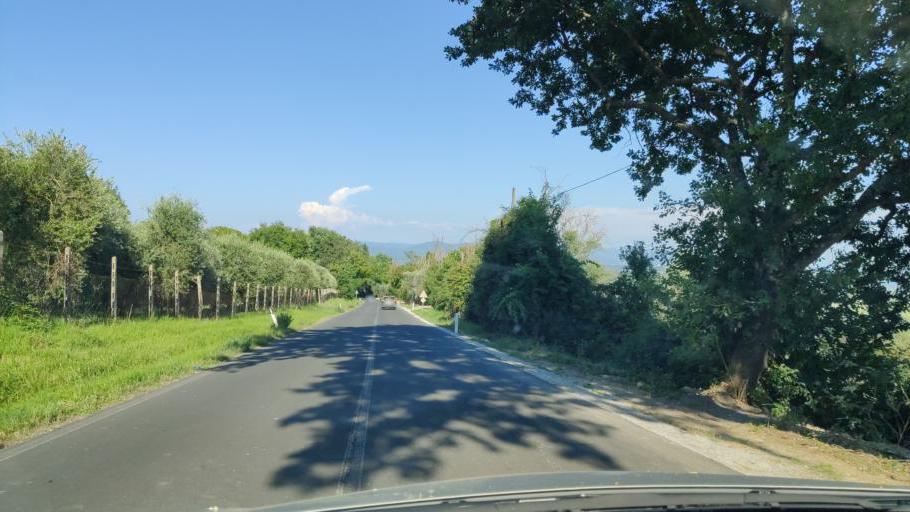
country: IT
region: Umbria
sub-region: Provincia di Terni
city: Penna in Teverina
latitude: 42.4882
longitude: 12.3557
